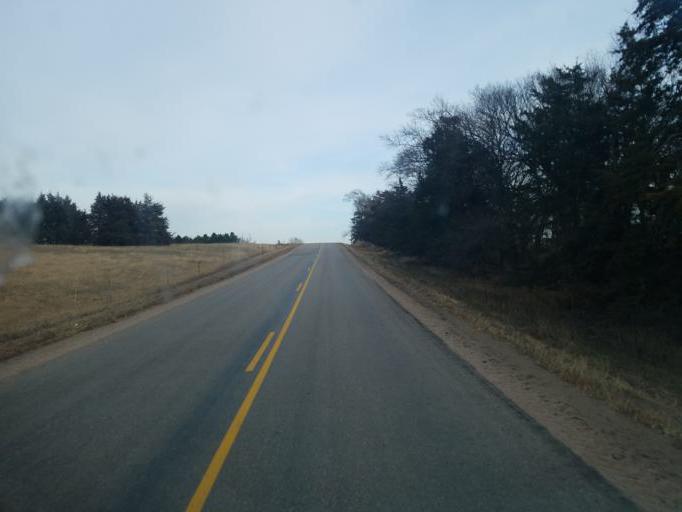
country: US
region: Nebraska
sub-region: Knox County
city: Creighton
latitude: 42.4660
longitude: -98.2220
